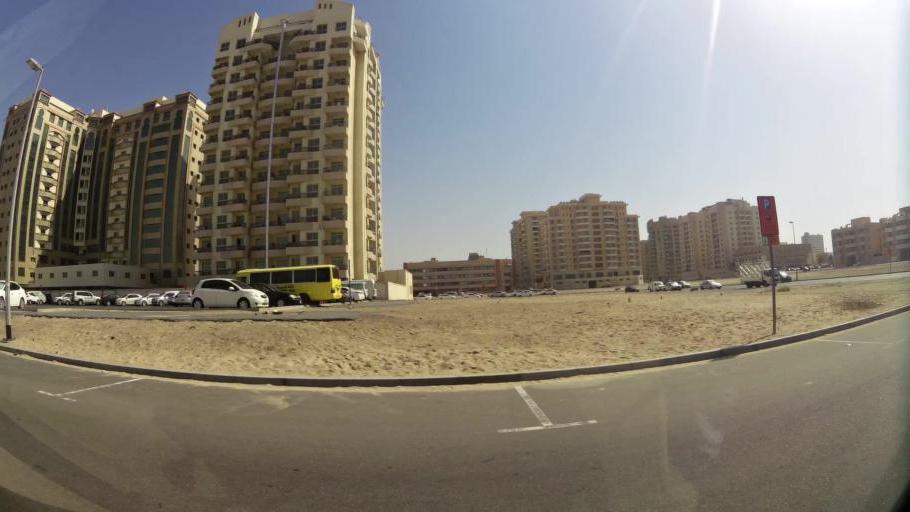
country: AE
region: Ash Shariqah
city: Sharjah
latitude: 25.2781
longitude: 55.3776
